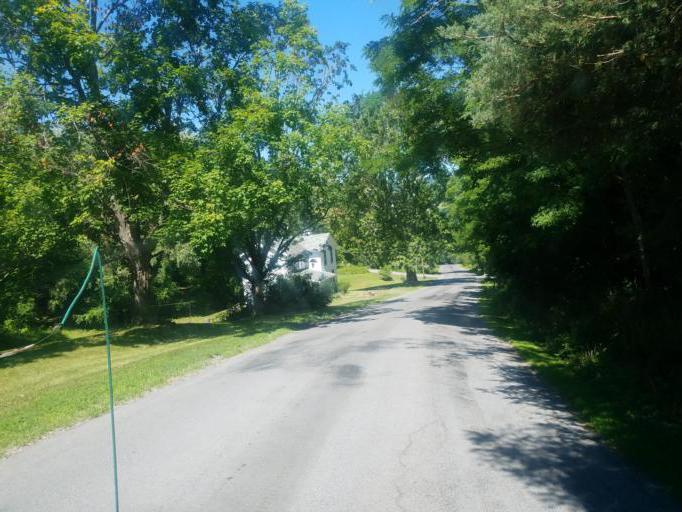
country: US
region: New York
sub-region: Ontario County
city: Naples
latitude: 42.7215
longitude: -77.3192
